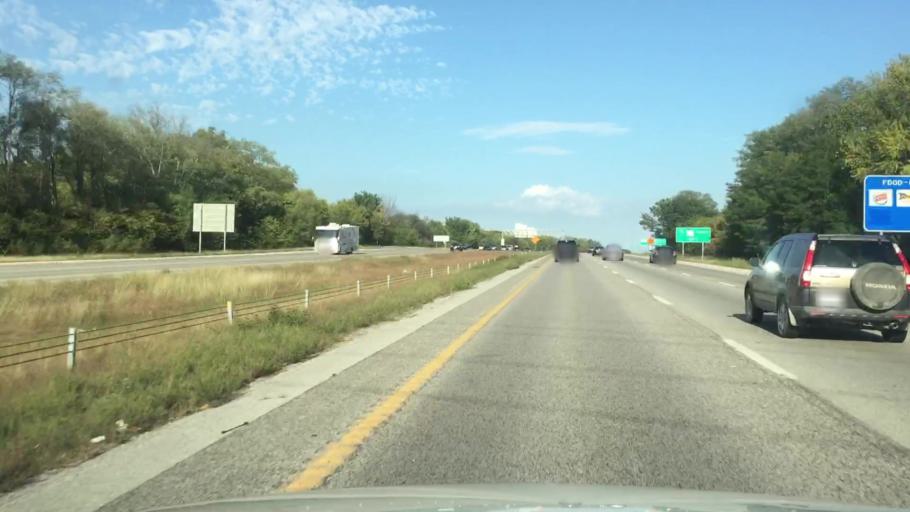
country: US
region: Missouri
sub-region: Jackson County
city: Lees Summit
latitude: 38.9406
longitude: -94.3919
